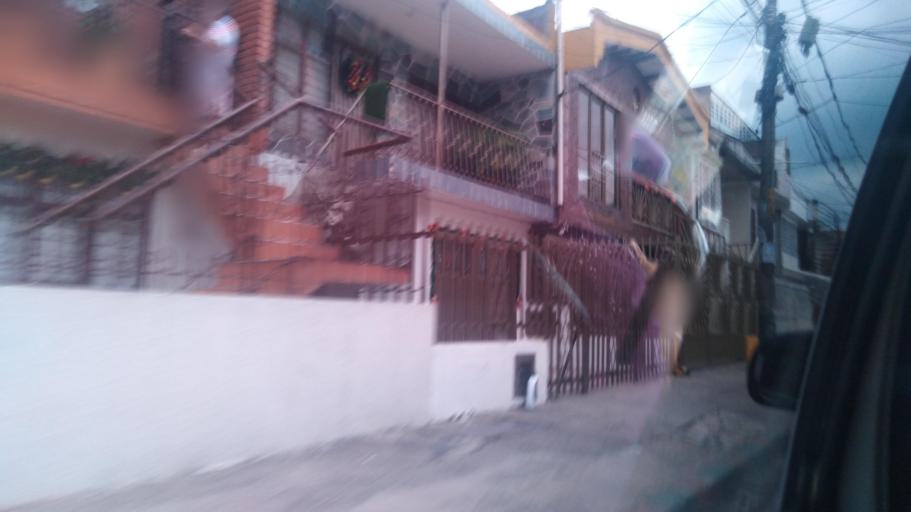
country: CO
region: Valle del Cauca
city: Cali
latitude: 3.4112
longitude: -76.5308
